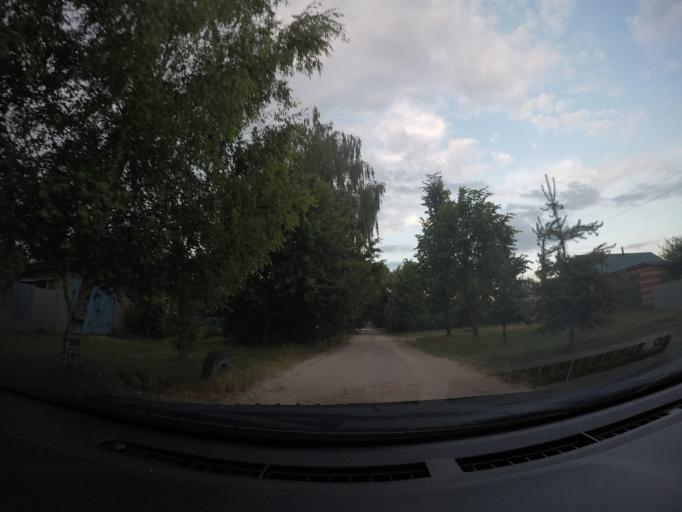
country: RU
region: Moskovskaya
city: Krasnyy Tkach
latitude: 55.3849
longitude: 39.2039
